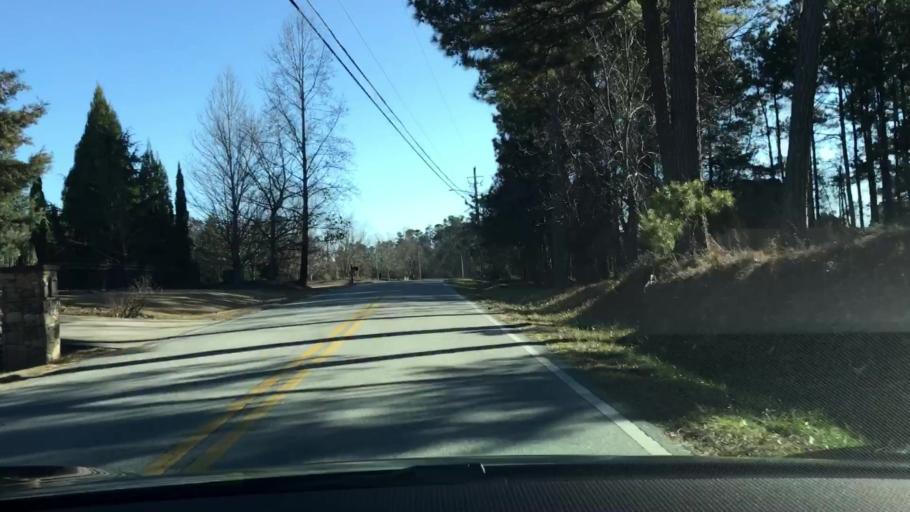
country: US
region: Georgia
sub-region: Gwinnett County
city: Buford
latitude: 34.1480
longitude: -84.0123
